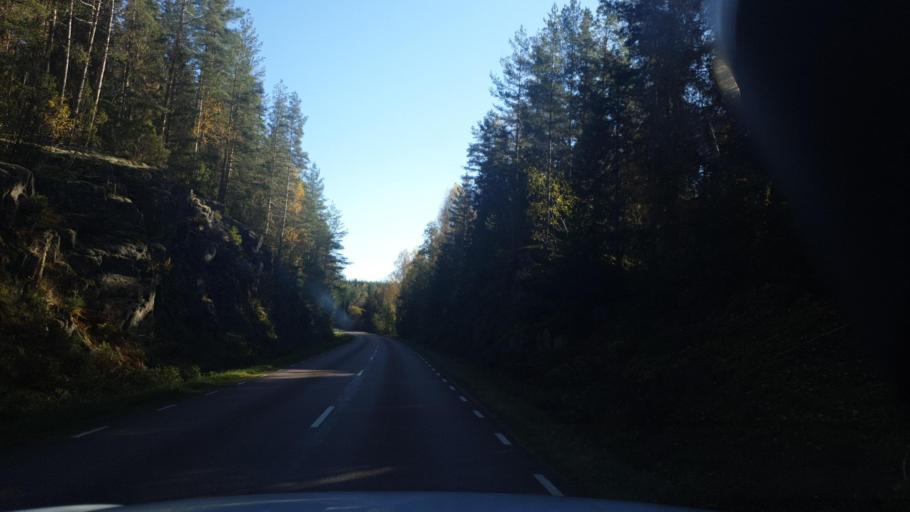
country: SE
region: Vaermland
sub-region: Grums Kommun
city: Slottsbron
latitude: 59.4062
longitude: 13.0061
